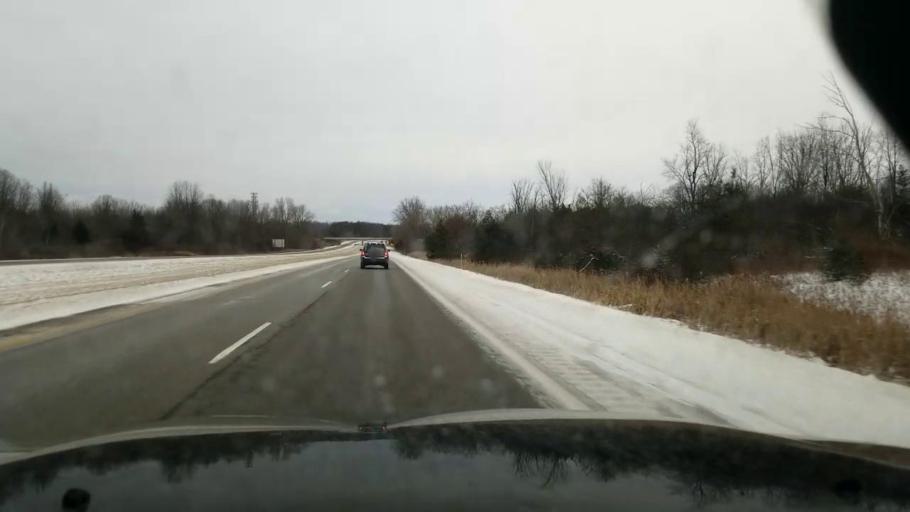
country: US
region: Michigan
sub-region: Jackson County
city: Jackson
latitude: 42.2386
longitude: -84.4755
